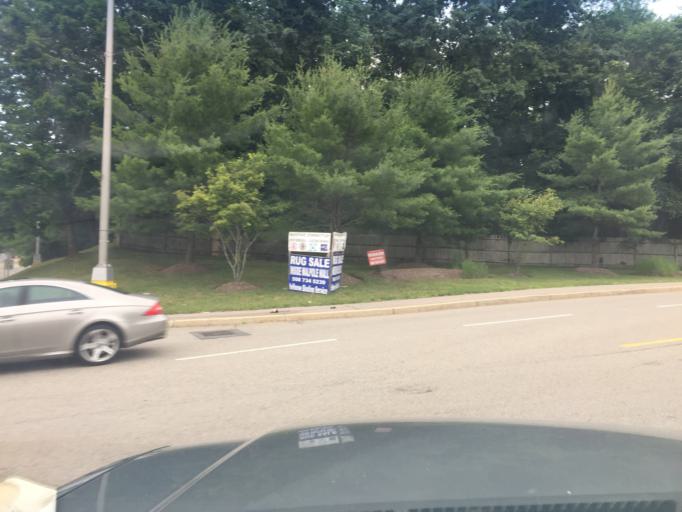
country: US
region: Massachusetts
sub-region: Norfolk County
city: Sharon
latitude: 42.1534
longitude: -71.2037
